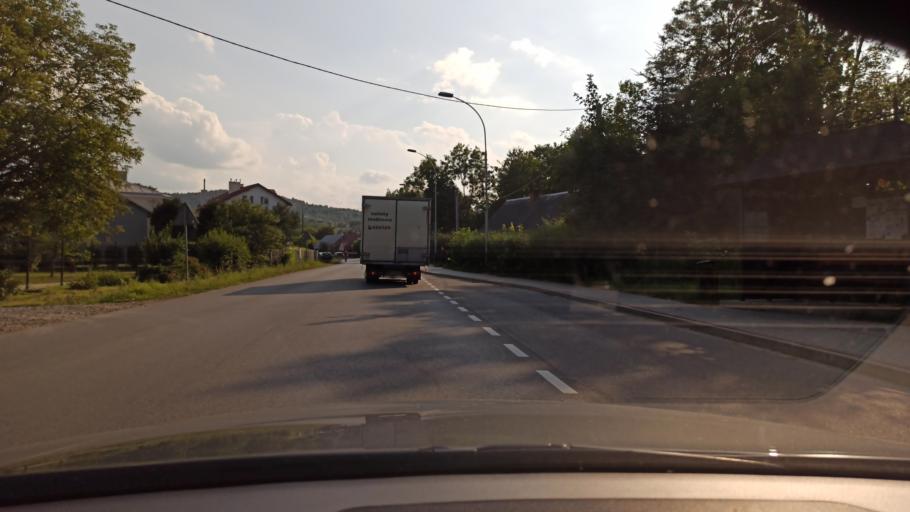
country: PL
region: Subcarpathian Voivodeship
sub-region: Powiat krosnienski
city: Iwonicz-Zdroj
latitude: 49.5969
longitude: 21.7990
